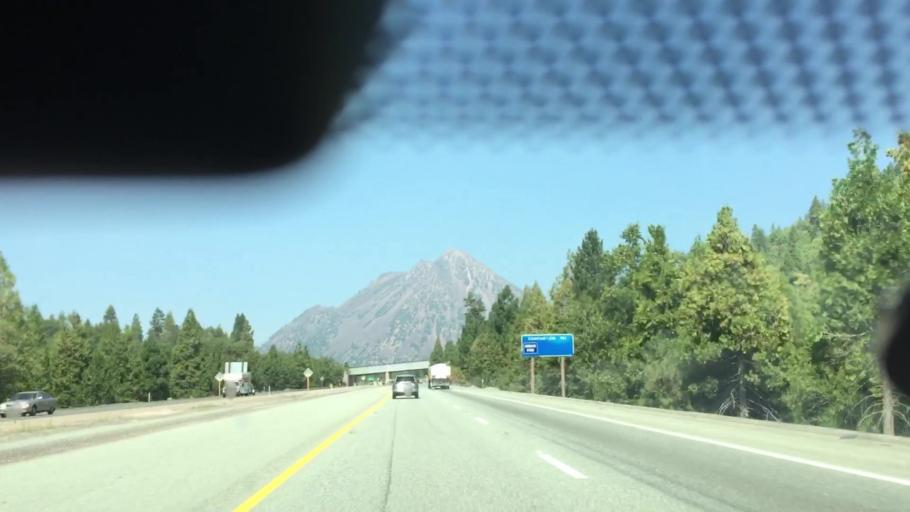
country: US
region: California
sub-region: Siskiyou County
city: Mount Shasta
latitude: 41.3234
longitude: -122.3309
